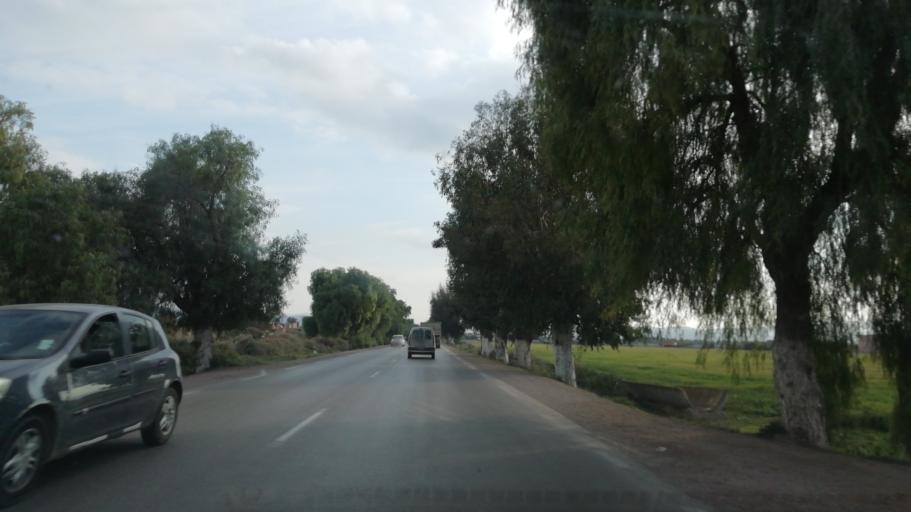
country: DZ
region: Mascara
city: Mascara
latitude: 35.6355
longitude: 0.0608
